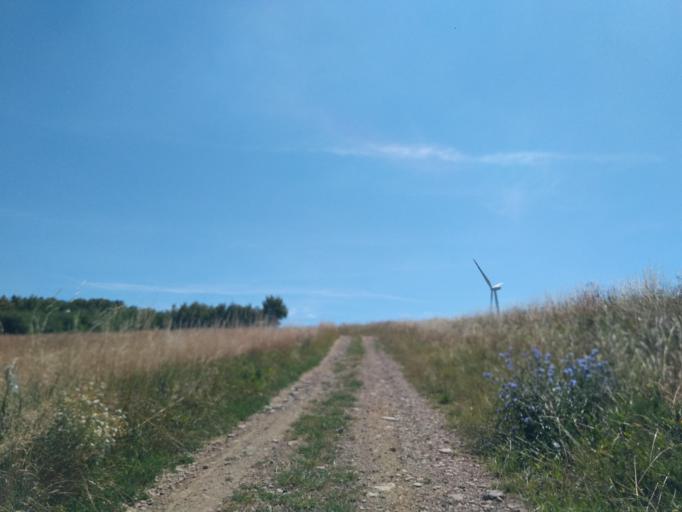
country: PL
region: Subcarpathian Voivodeship
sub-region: Powiat sanocki
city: Bukowsko
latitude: 49.5150
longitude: 22.0475
